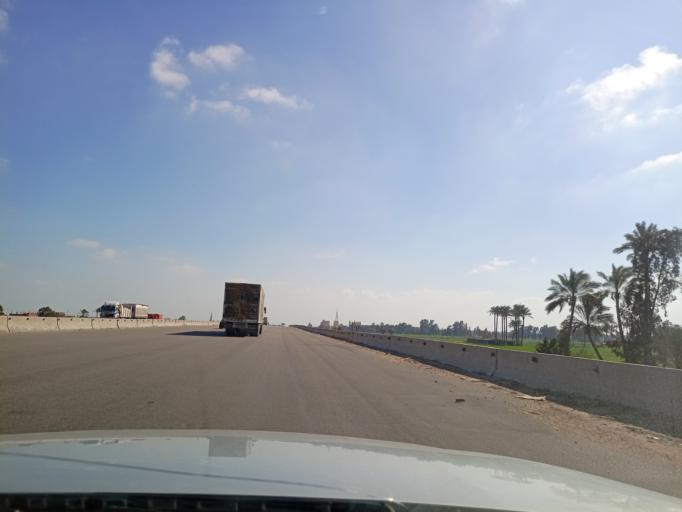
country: EG
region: Eastern Province
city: Mashtul as Suq
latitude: 30.4630
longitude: 31.3214
